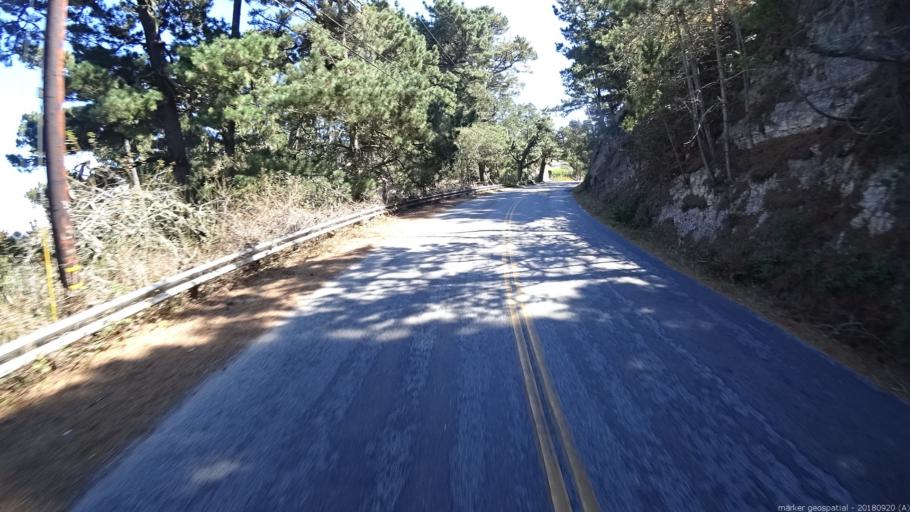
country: US
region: California
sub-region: Monterey County
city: Carmel-by-the-Sea
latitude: 36.5701
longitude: -121.9006
